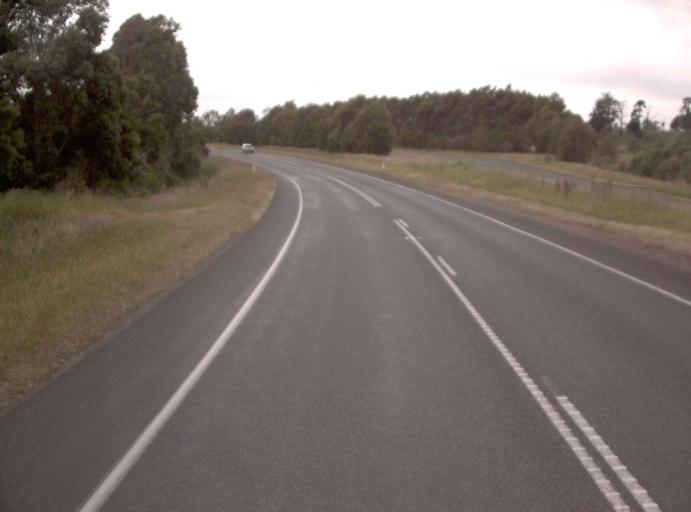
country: AU
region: Victoria
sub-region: Bass Coast
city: North Wonthaggi
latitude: -38.3719
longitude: 145.6810
